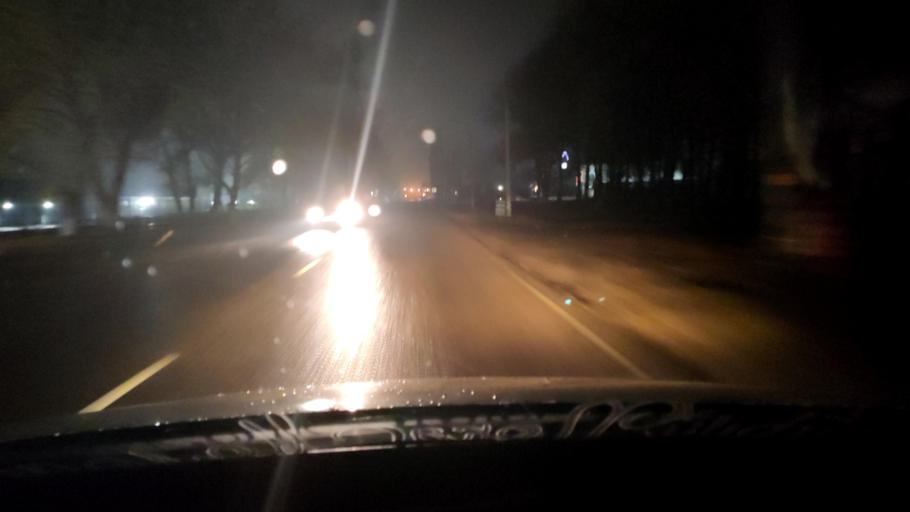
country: RU
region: Voronezj
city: Semiluki
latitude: 51.6900
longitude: 38.9920
